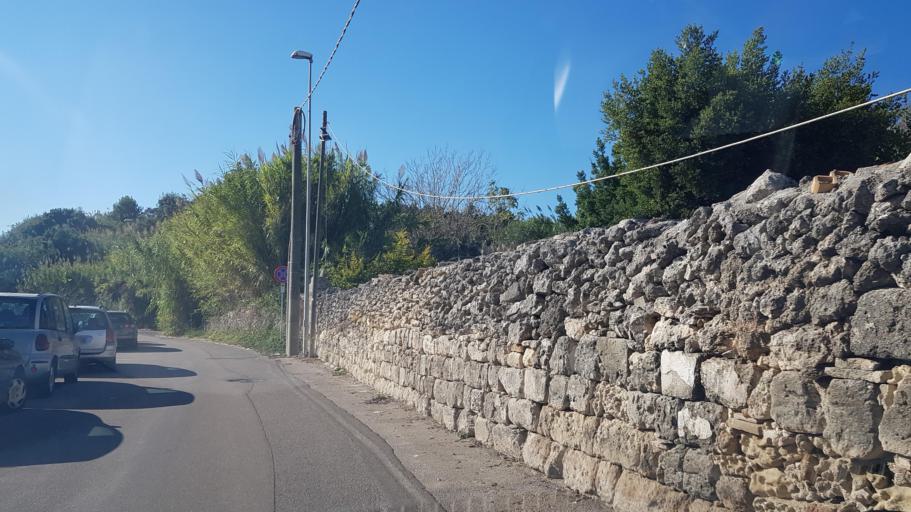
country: IT
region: Apulia
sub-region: Provincia di Lecce
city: Otranto
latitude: 40.1471
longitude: 18.4845
